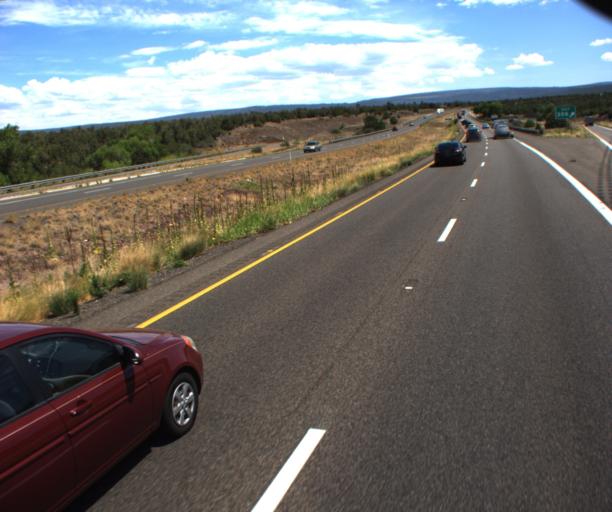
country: US
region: Arizona
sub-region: Yavapai County
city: Village of Oak Creek (Big Park)
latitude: 34.7622
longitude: -111.6588
